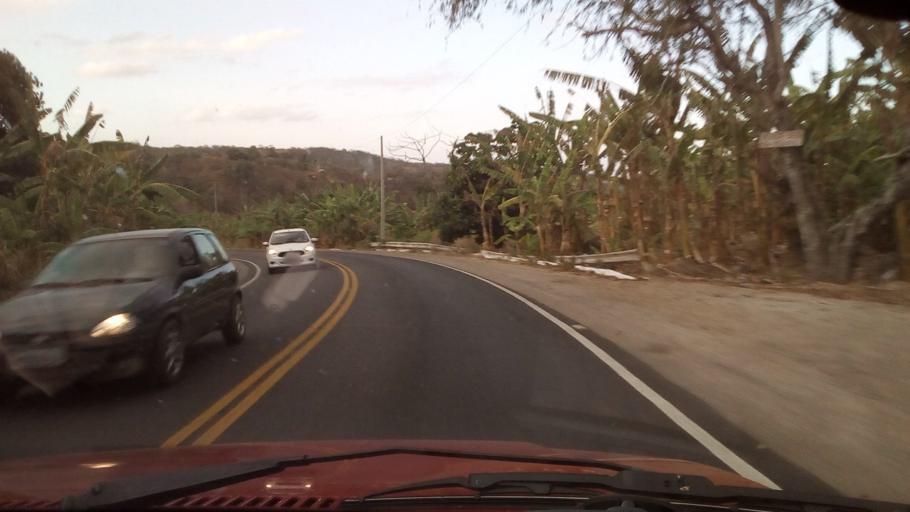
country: BR
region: Paraiba
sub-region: Bananeiras
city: Solanea
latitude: -6.7453
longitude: -35.5629
